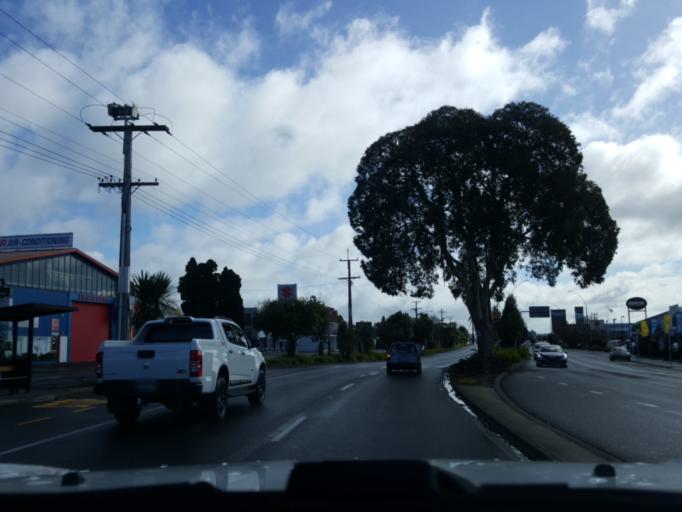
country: NZ
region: Waikato
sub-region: Hamilton City
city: Hamilton
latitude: -37.7645
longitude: 175.2528
